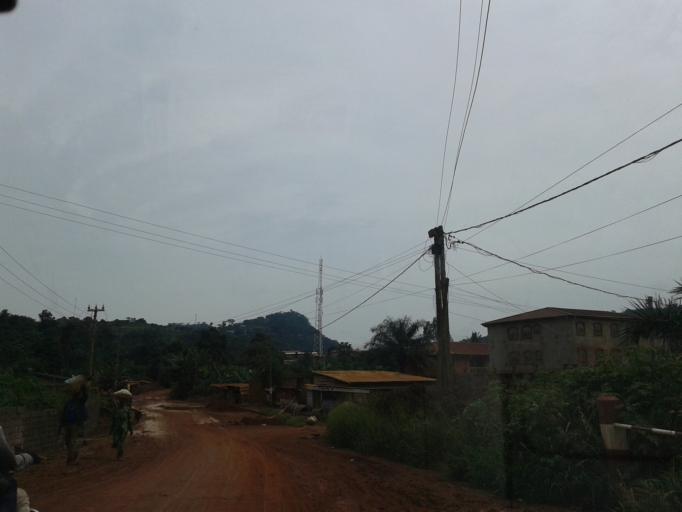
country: CM
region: Centre
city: Yaounde
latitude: 3.9248
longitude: 11.5143
